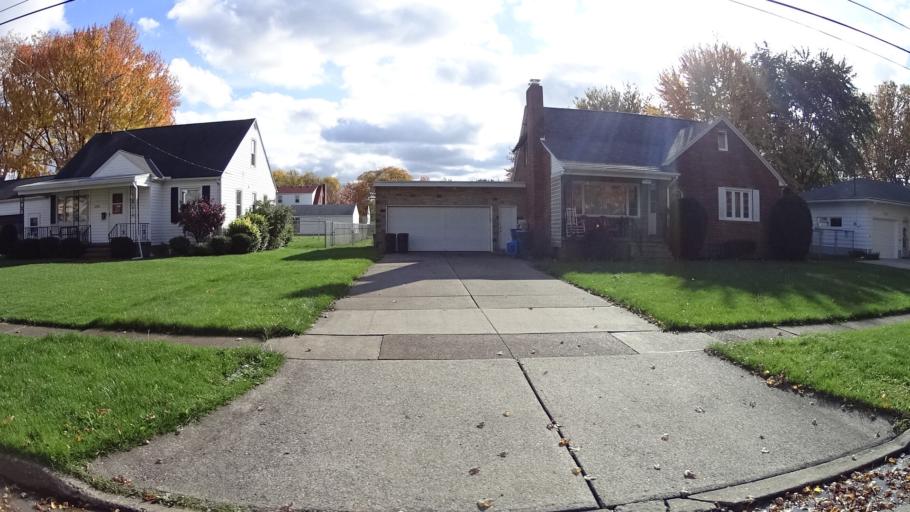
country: US
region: Ohio
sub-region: Lorain County
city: Lorain
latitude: 41.4407
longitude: -82.1871
